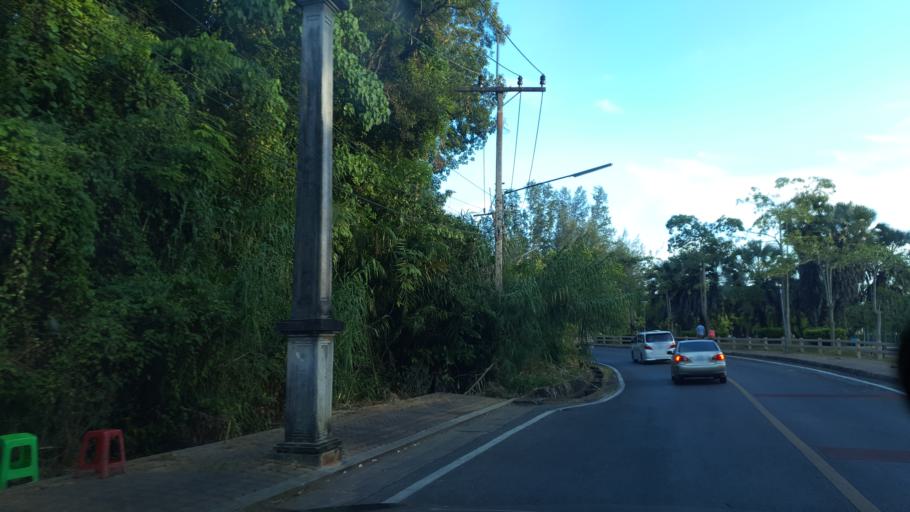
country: TH
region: Krabi
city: Krabi
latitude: 8.0532
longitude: 98.9168
